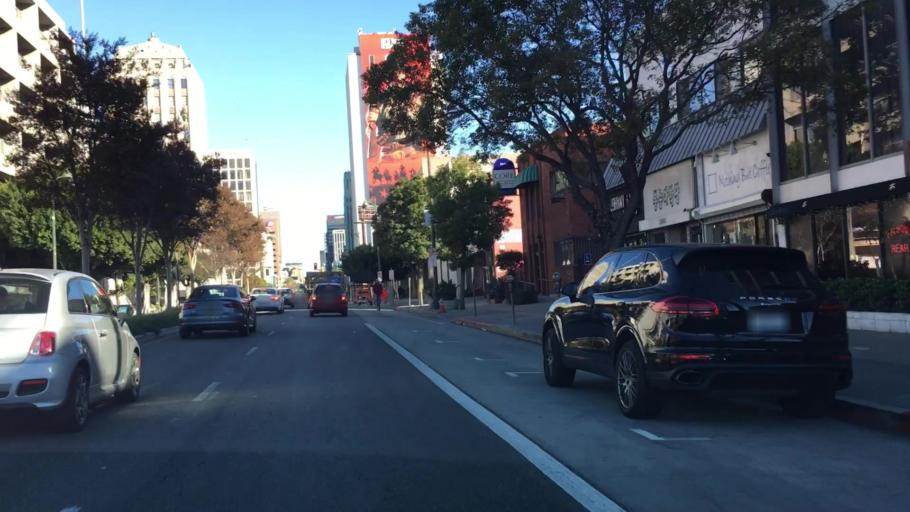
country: US
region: California
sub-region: Los Angeles County
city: Hollywood
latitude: 34.0617
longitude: -118.3133
